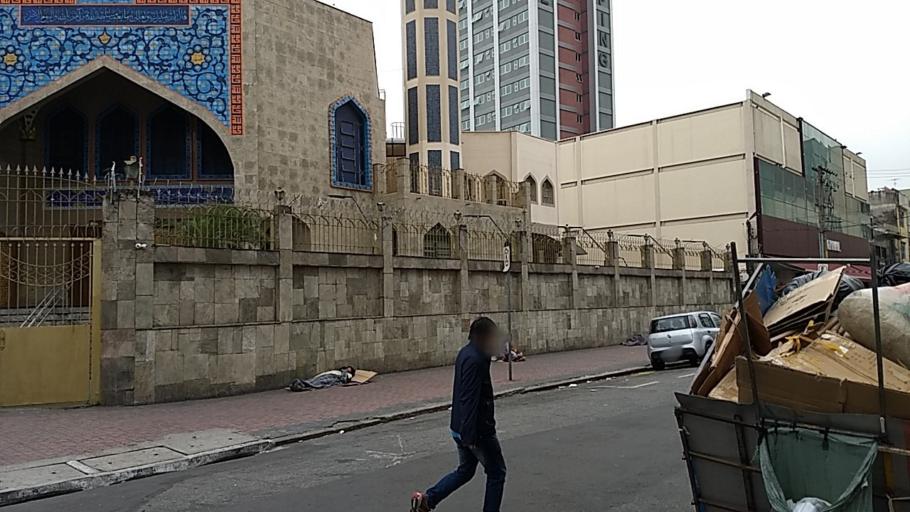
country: BR
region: Sao Paulo
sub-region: Sao Paulo
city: Sao Paulo
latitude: -23.5361
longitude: -46.6222
